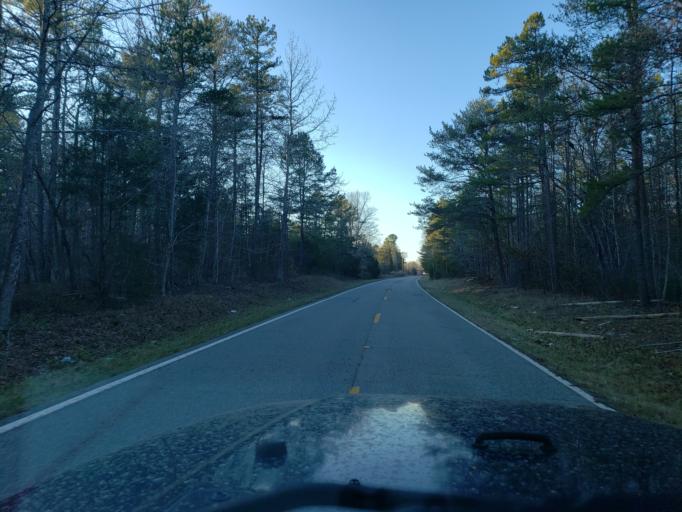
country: US
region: South Carolina
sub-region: Cherokee County
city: Blacksburg
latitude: 35.0618
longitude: -81.4294
